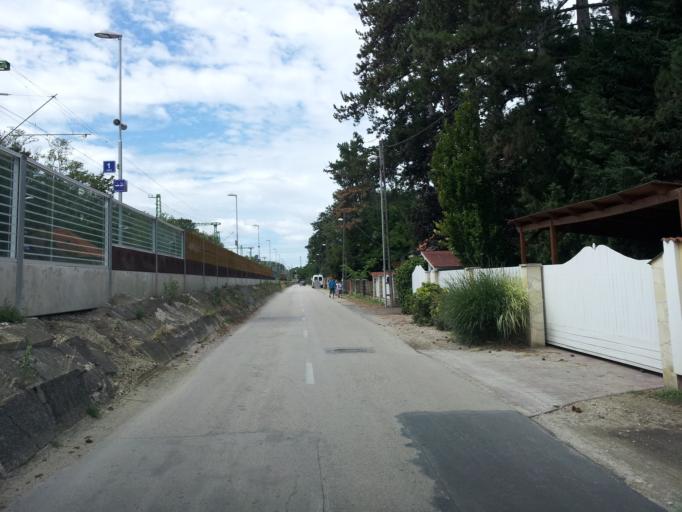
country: HU
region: Somogy
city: Balatonszabadi
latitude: 46.9358
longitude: 18.1218
